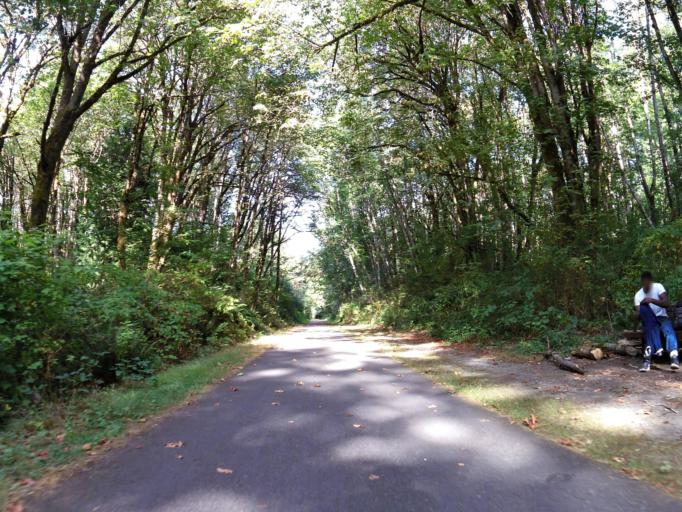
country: US
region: Washington
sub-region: Thurston County
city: Olympia
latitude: 47.0337
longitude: -122.8797
